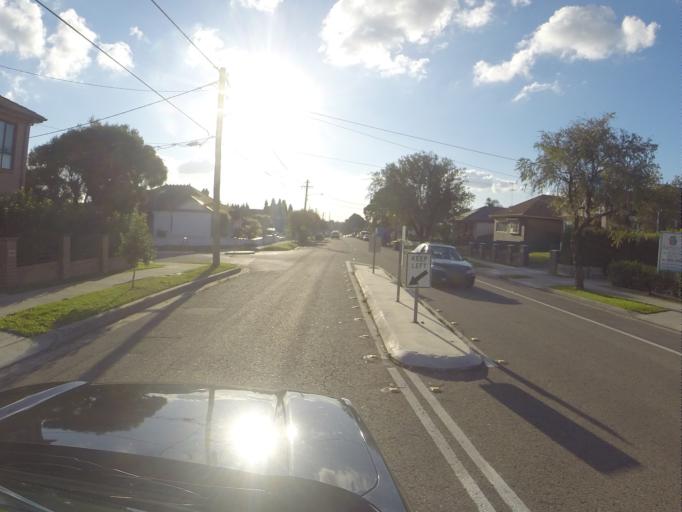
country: AU
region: New South Wales
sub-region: Rockdale
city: Bexley
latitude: -33.9533
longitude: 151.1180
